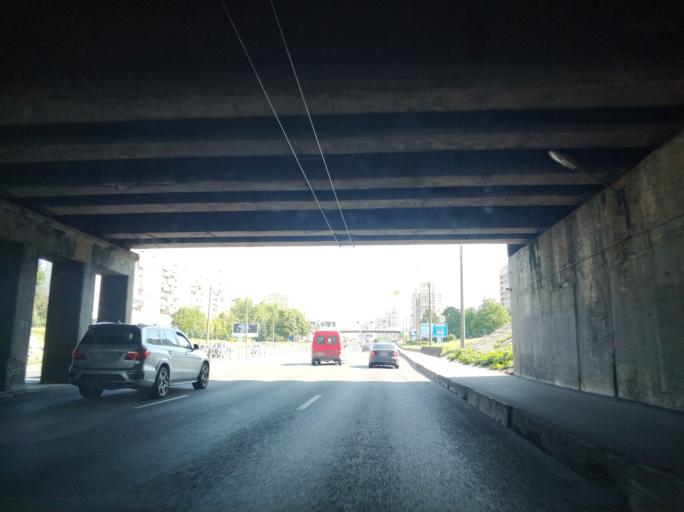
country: RU
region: St.-Petersburg
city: Kupchino
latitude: 59.8539
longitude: 30.3642
